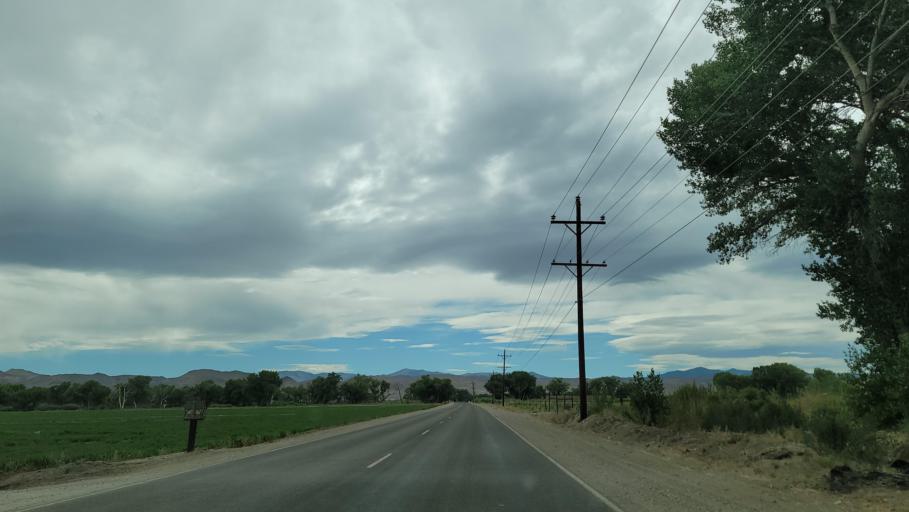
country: US
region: Nevada
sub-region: Lyon County
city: Yerington
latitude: 39.0482
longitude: -119.1574
